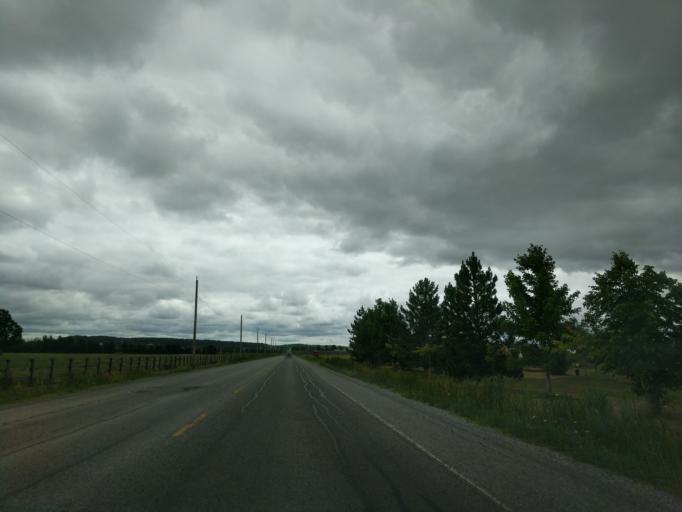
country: CA
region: Ontario
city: Thorold
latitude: 43.1769
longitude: -79.1689
